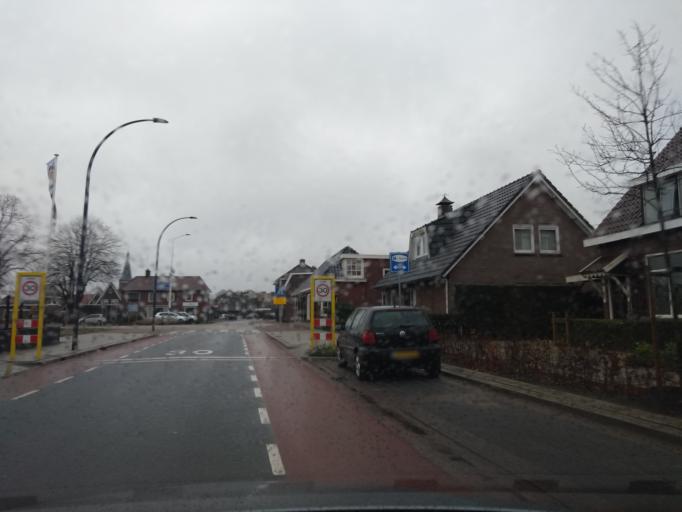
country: NL
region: Overijssel
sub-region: Gemeente Wierden
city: Wierden
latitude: 52.3590
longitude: 6.5875
